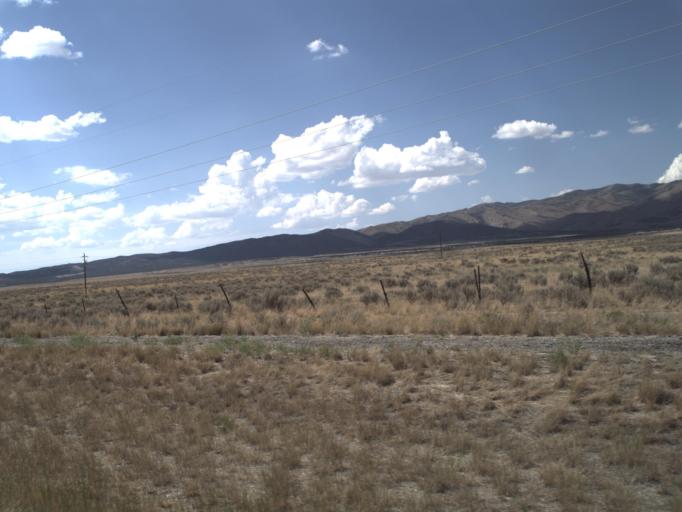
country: US
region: Idaho
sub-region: Oneida County
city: Malad City
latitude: 41.9657
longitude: -113.0631
